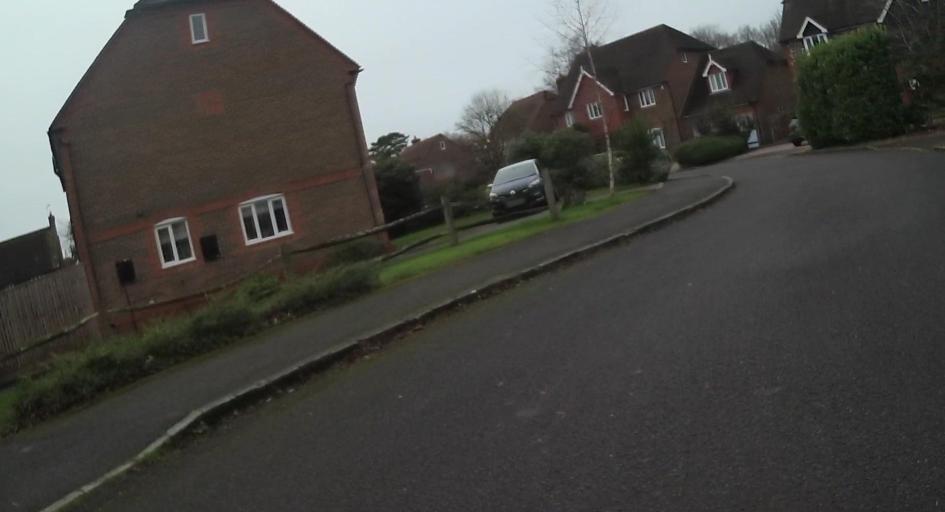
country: GB
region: England
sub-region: Hampshire
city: Four Marks
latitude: 51.1083
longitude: -1.0577
